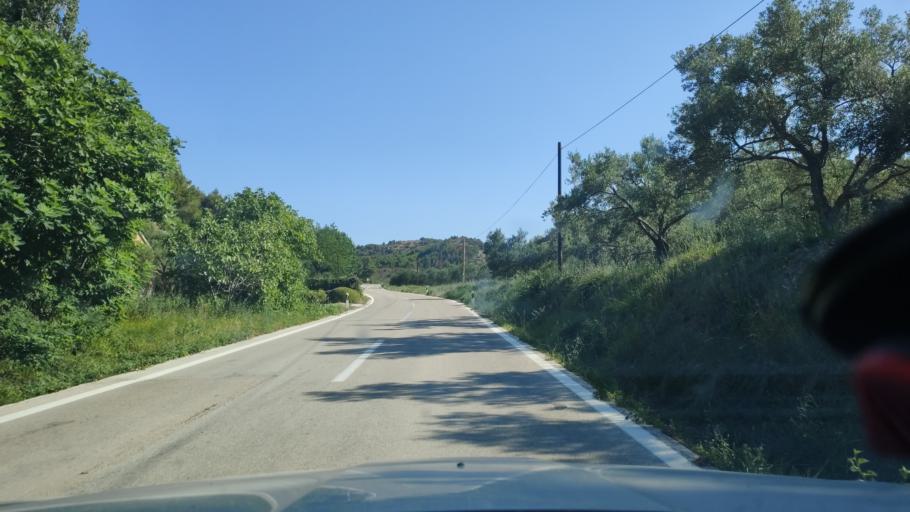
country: HR
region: Sibensko-Kniniska
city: Zaton
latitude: 43.8511
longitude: 15.8973
